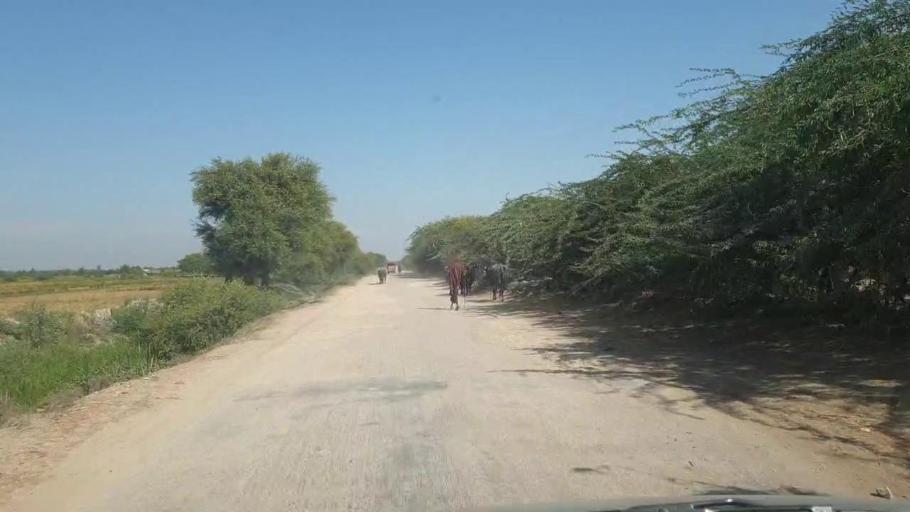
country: PK
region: Sindh
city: Tando Bago
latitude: 24.8015
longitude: 68.9777
